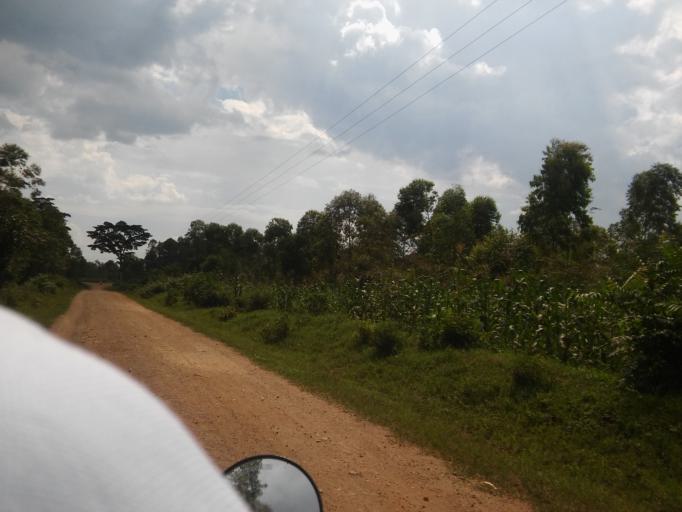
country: UG
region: Eastern Region
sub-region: Mbale District
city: Mbale
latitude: 1.0552
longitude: 34.1820
